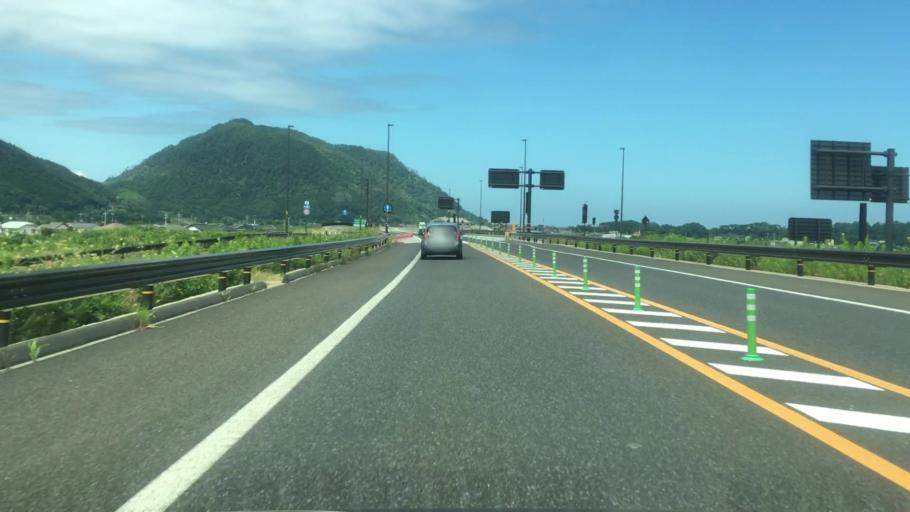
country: JP
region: Tottori
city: Tottori
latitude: 35.5730
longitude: 134.3146
